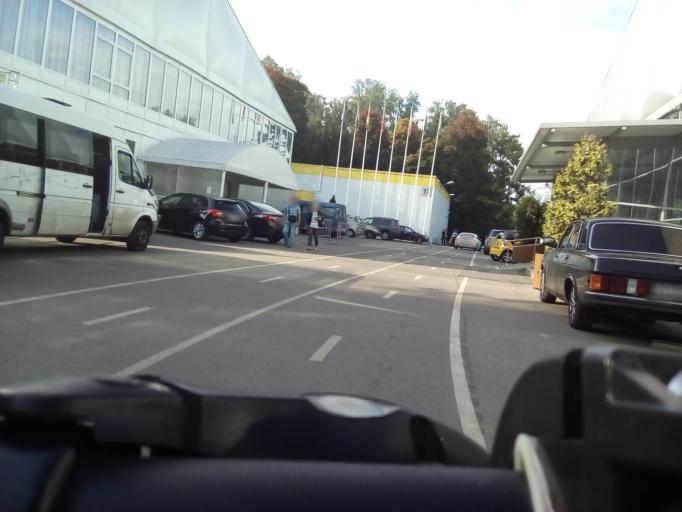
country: RU
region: Moscow
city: Sokol'niki
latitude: 55.7996
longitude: 37.6734
